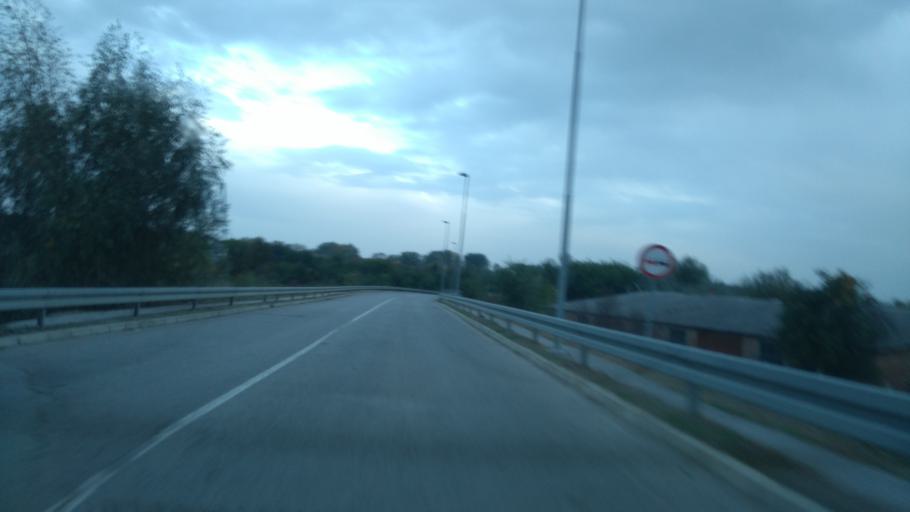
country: RS
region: Autonomna Pokrajina Vojvodina
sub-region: Severnobanatski Okrug
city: Ada
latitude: 45.7861
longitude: 20.1379
